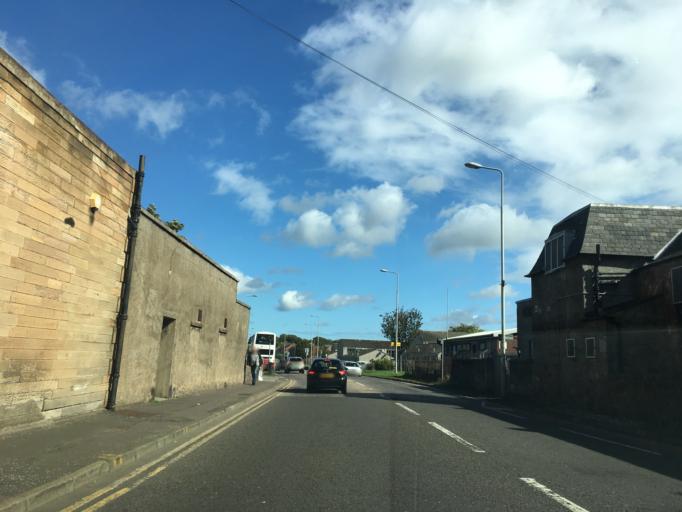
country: GB
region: Scotland
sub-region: Midlothian
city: Loanhead
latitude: 55.9061
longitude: -3.1333
